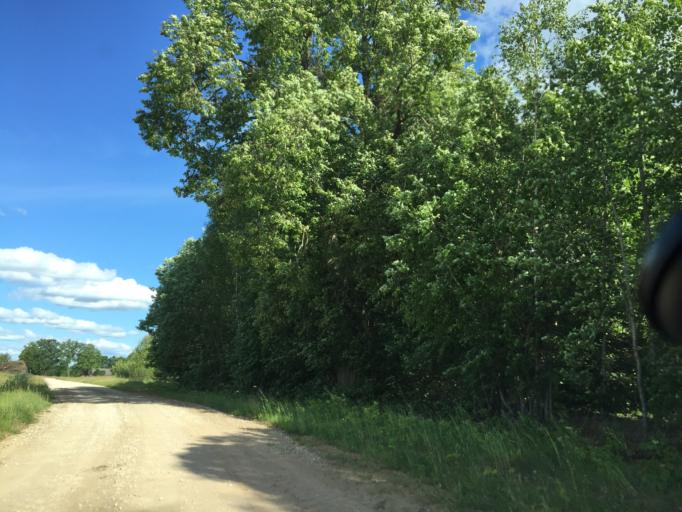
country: LV
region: Vecumnieki
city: Vecumnieki
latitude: 56.4184
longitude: 24.6151
